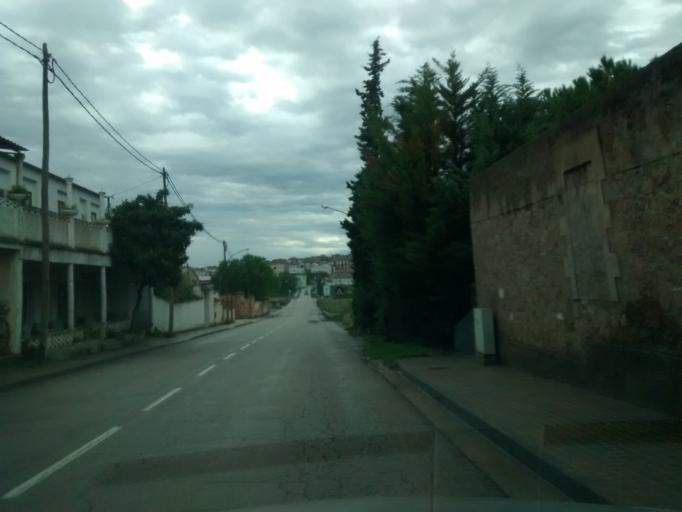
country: ES
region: Aragon
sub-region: Provincia de Zaragoza
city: Maella
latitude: 41.1177
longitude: 0.1453
